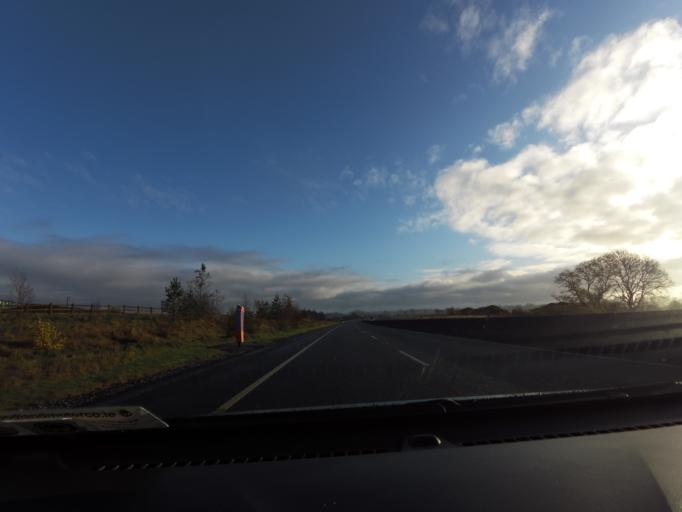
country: IE
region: Connaught
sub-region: County Galway
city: Loughrea
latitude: 53.2756
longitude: -8.5555
